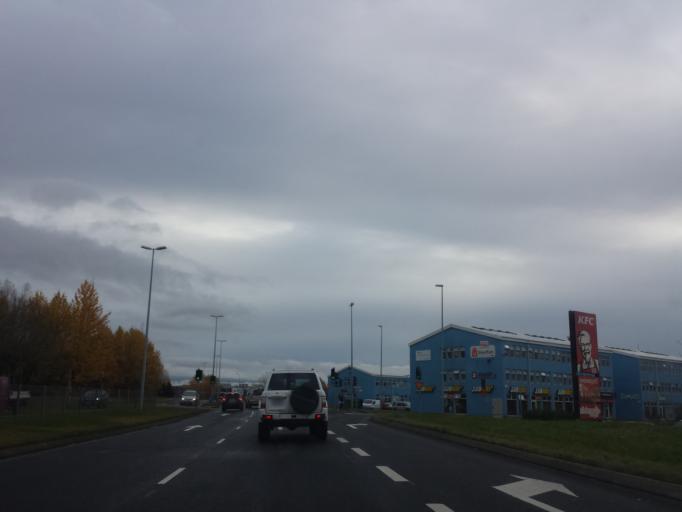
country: IS
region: Capital Region
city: Reykjavik
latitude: 64.1320
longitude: -21.8670
